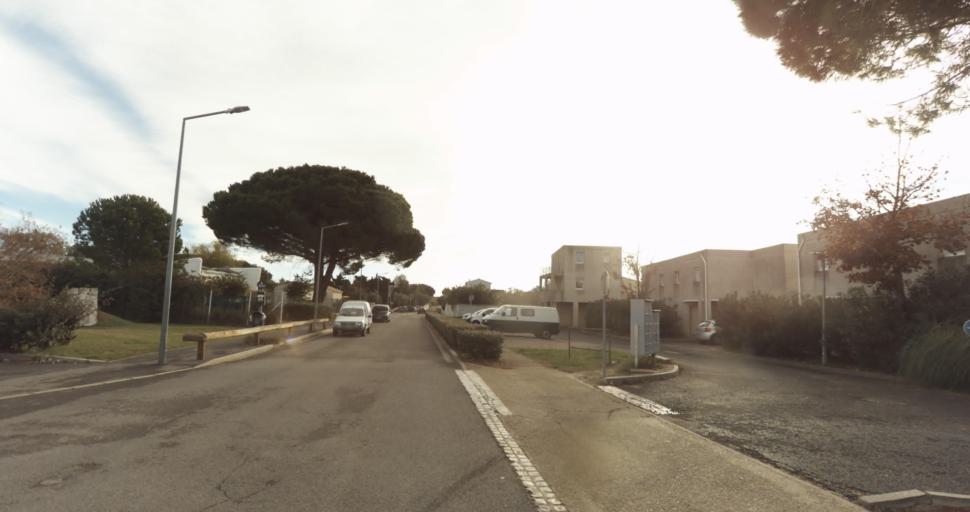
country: FR
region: Languedoc-Roussillon
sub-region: Departement du Gard
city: Aigues-Mortes
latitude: 43.5674
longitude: 4.2006
